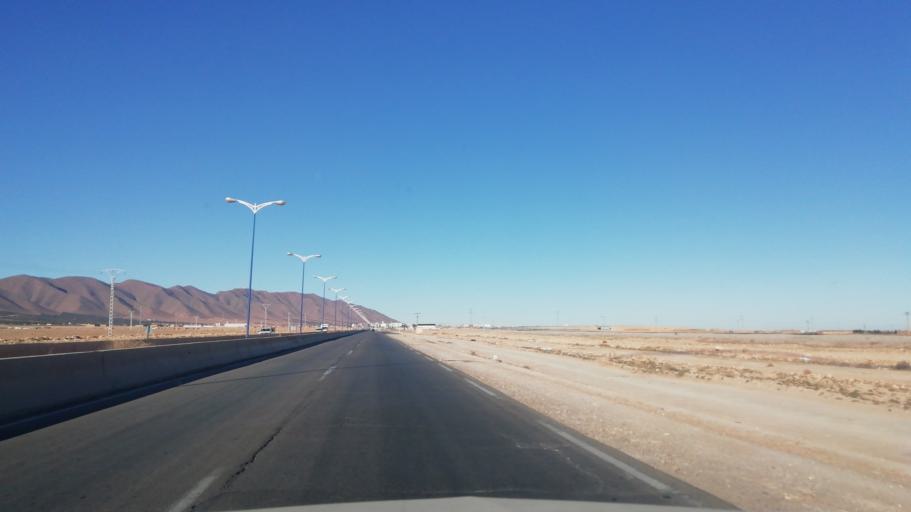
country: DZ
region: Wilaya de Naama
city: Naama
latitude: 33.4999
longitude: -0.2882
